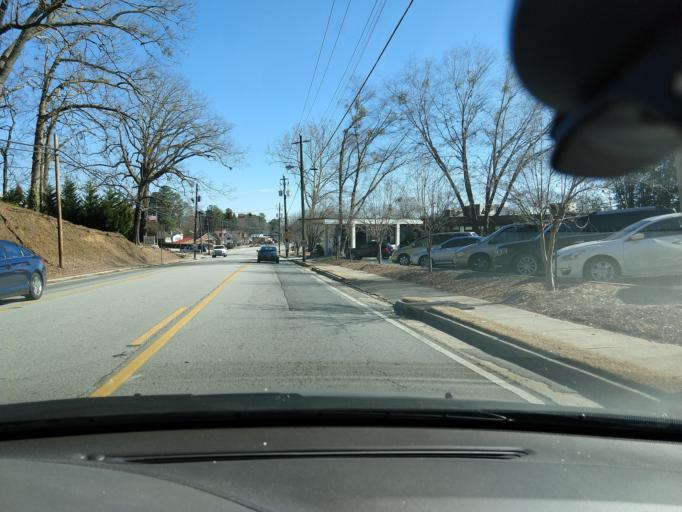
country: US
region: Georgia
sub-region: Stephens County
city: Toccoa
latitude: 34.5804
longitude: -83.3184
